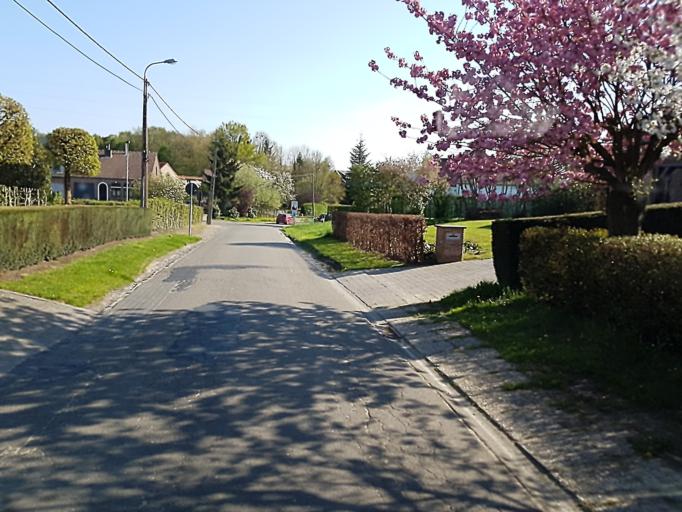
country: BE
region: Flanders
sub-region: Provincie Oost-Vlaanderen
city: Temse
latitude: 51.1352
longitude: 4.2226
